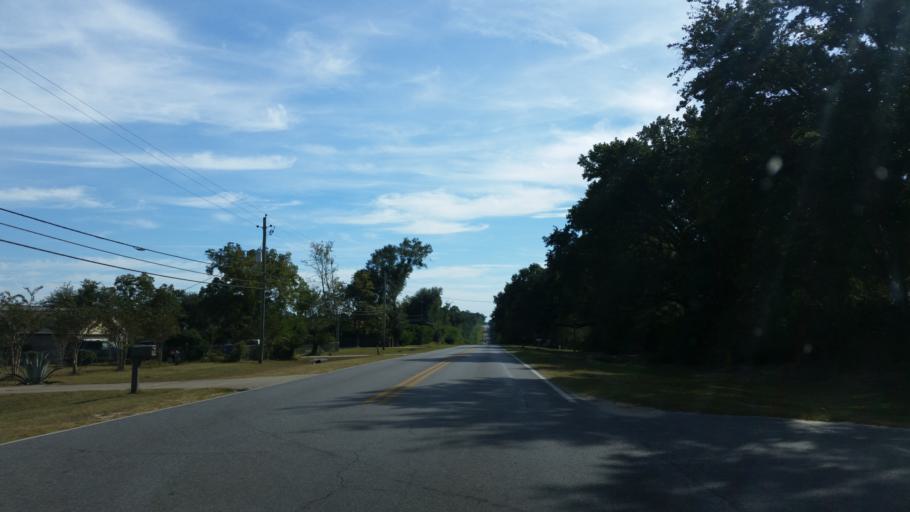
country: US
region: Florida
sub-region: Escambia County
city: Gonzalez
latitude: 30.5802
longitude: -87.2610
